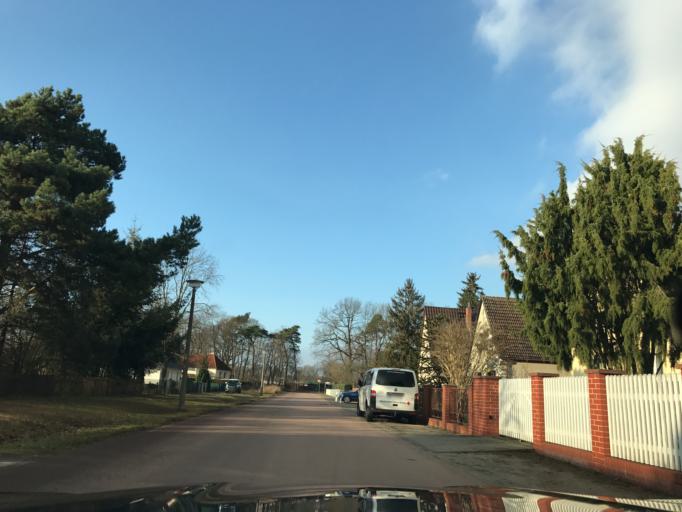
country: DE
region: Brandenburg
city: Brandenburg an der Havel
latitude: 52.3784
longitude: 12.5211
